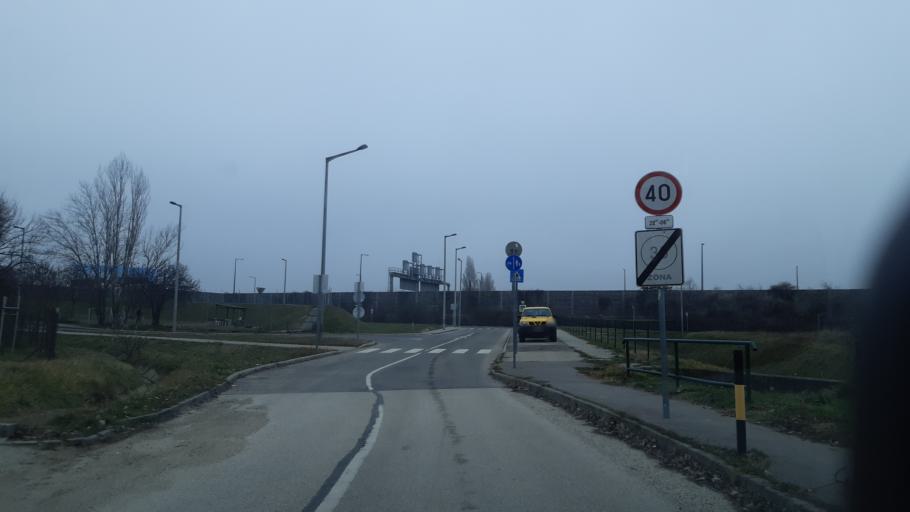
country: HU
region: Pest
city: Budaors
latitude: 47.4560
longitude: 18.9732
